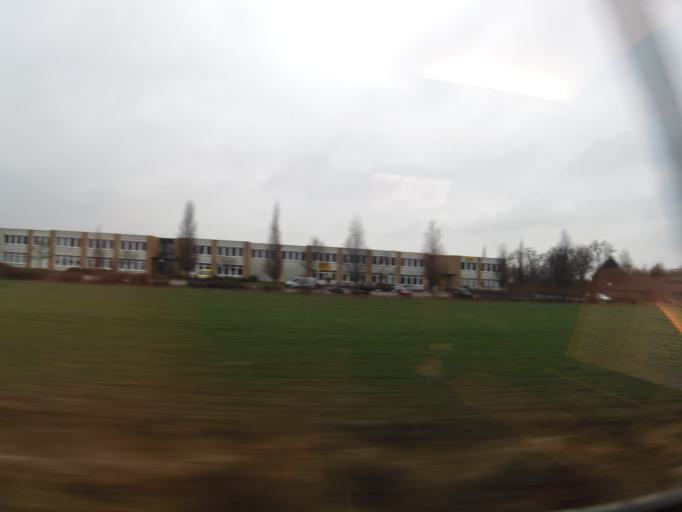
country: DE
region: Saxony
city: Zwochau
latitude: 51.4147
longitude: 12.3008
